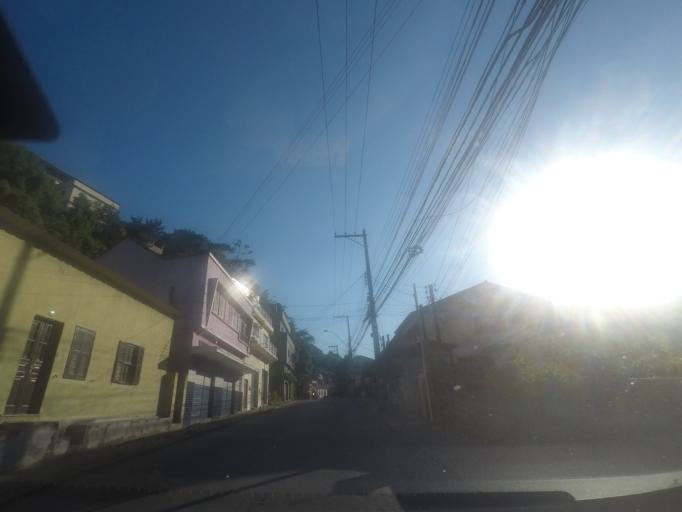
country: BR
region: Rio de Janeiro
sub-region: Petropolis
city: Petropolis
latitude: -22.4932
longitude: -43.1581
